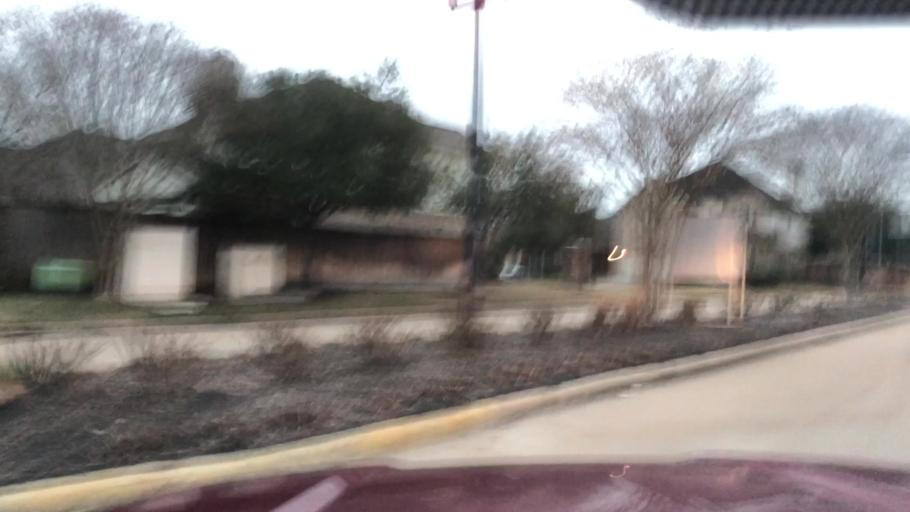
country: US
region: Texas
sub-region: Harris County
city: Tomball
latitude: 30.0861
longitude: -95.5557
